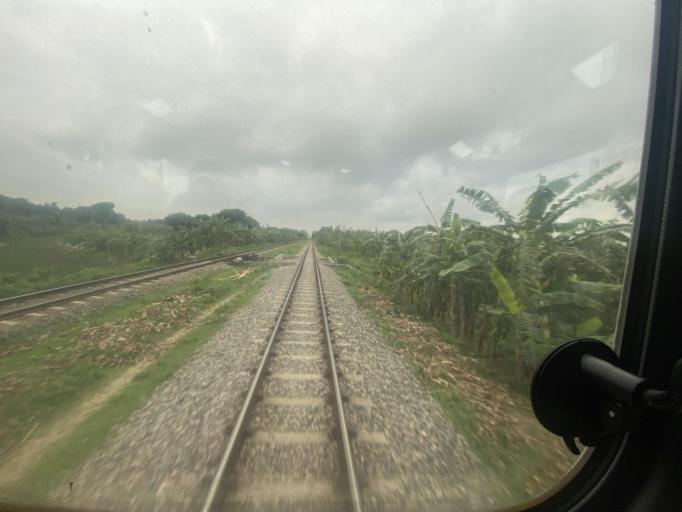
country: BD
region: Dhaka
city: Narsingdi
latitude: 23.9307
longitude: 90.6848
